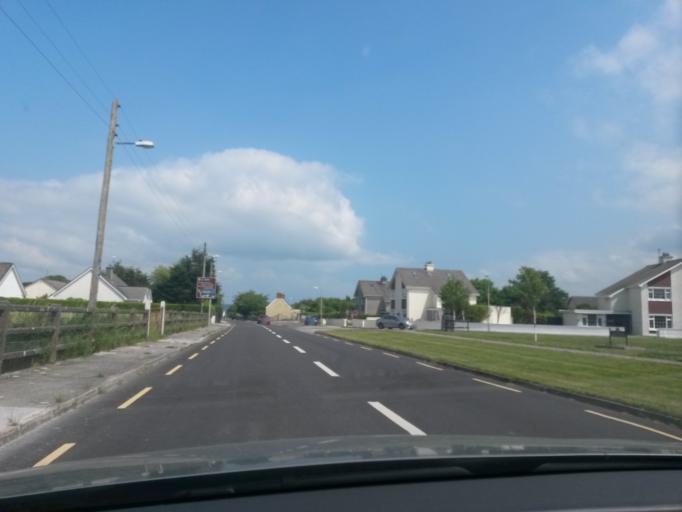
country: IE
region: Munster
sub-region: An Clar
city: Kilrush
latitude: 52.5719
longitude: -9.3815
